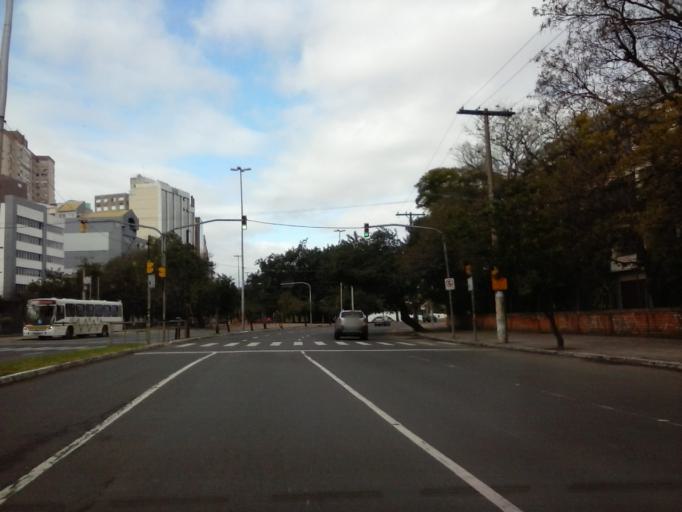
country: BR
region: Rio Grande do Sul
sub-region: Porto Alegre
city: Porto Alegre
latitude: -30.0375
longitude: -51.2316
